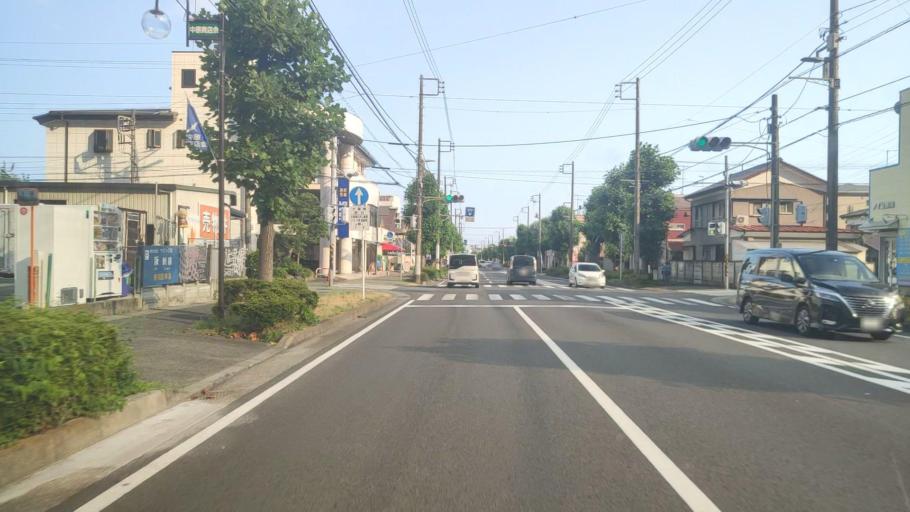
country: JP
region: Kanagawa
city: Hiratsuka
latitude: 35.3458
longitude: 139.3337
